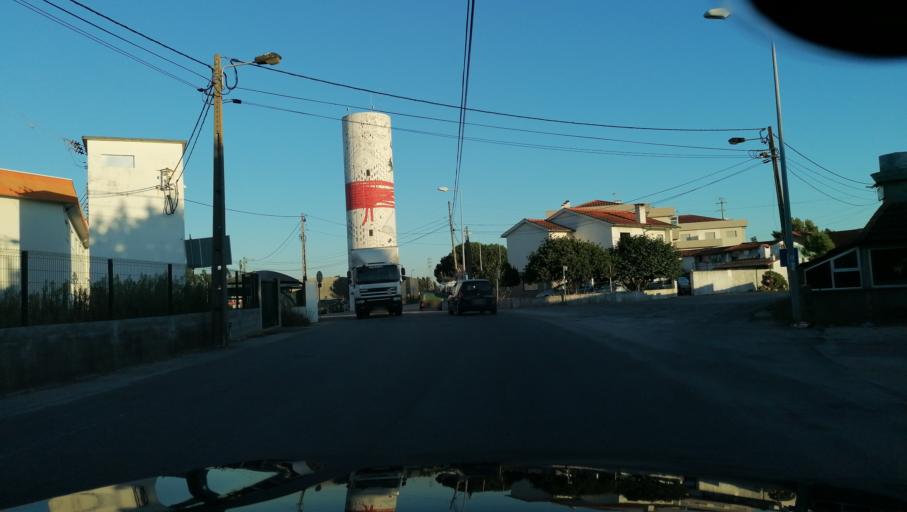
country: PT
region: Aveiro
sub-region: Agueda
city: Agueda
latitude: 40.5578
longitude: -8.4664
